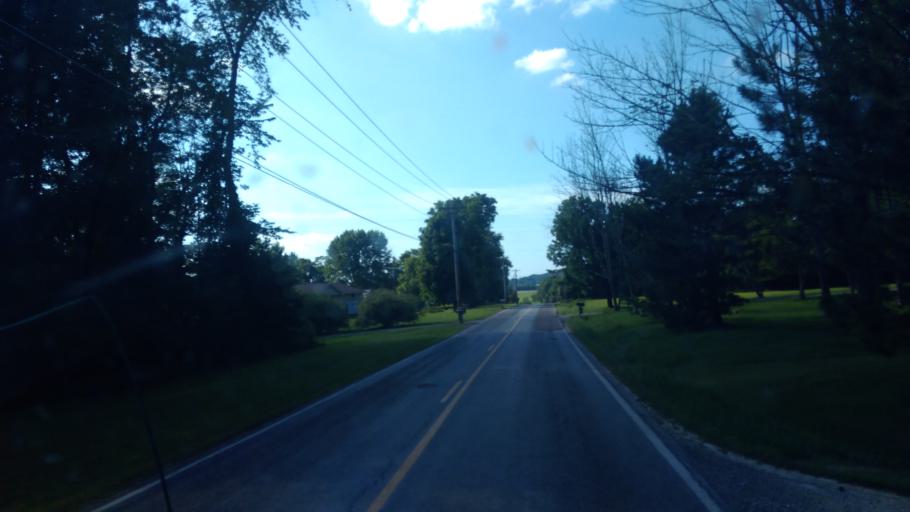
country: US
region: Ohio
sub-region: Wayne County
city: Shreve
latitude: 40.7164
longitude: -82.0512
